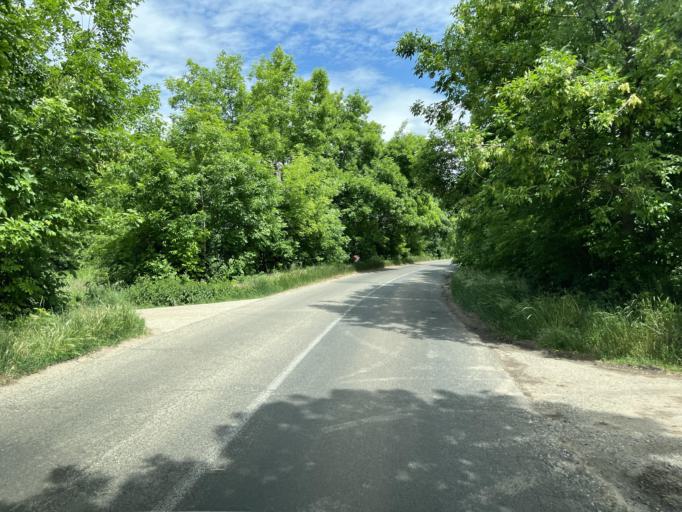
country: HU
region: Pest
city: Toalmas
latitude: 47.4908
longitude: 19.6439
